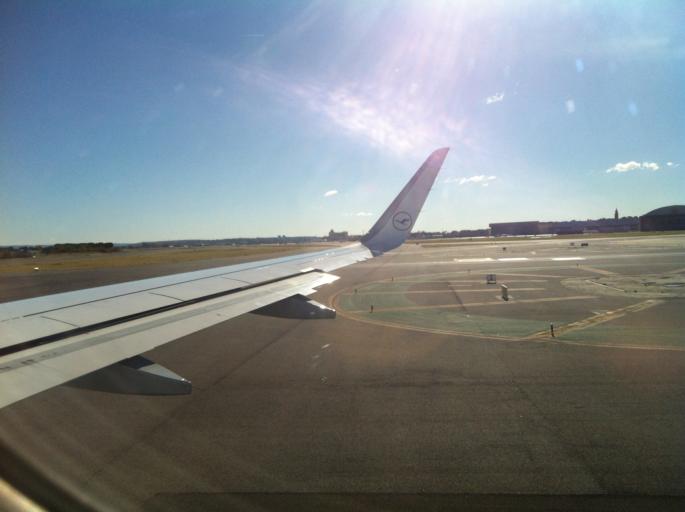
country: ES
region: Madrid
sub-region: Provincia de Madrid
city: Barajas de Madrid
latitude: 40.4886
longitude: -3.5727
